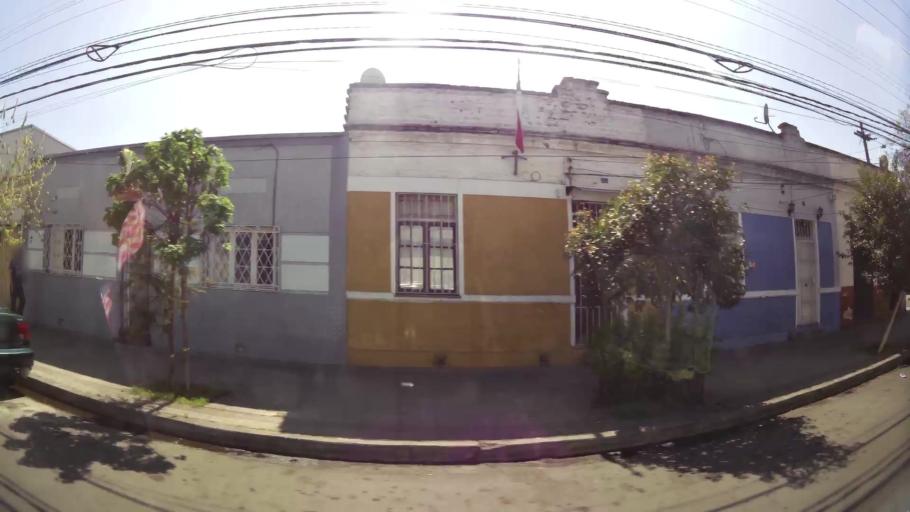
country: CL
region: Santiago Metropolitan
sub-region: Provincia de Santiago
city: Santiago
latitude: -33.4654
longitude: -70.6319
